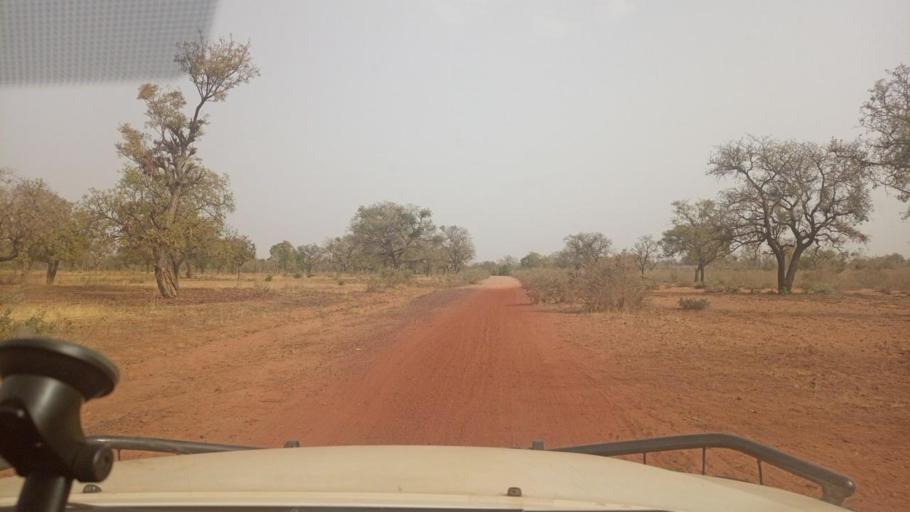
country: BF
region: Boucle du Mouhoun
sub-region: Province des Banwa
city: Salanso
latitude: 12.0977
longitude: -4.3325
